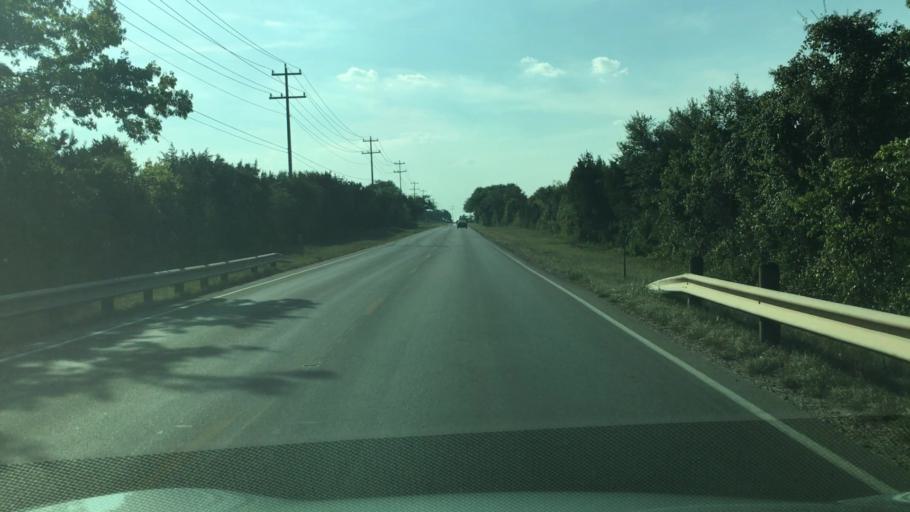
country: US
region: Texas
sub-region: Hays County
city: Buda
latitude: 30.0978
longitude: -97.9323
